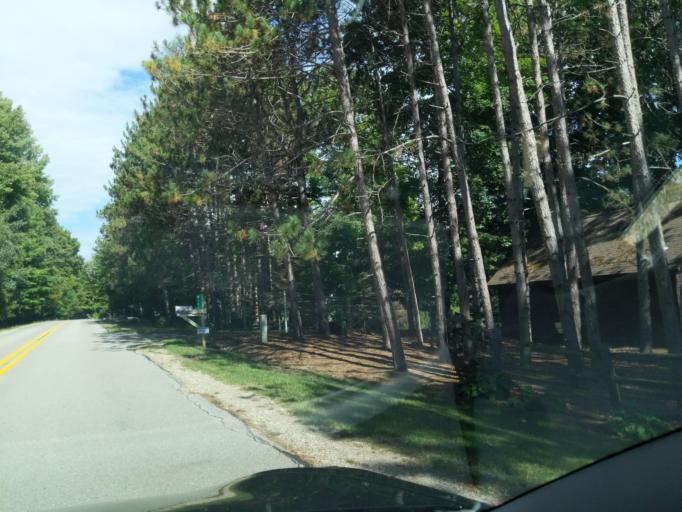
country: US
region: Michigan
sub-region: Antrim County
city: Bellaire
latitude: 44.9701
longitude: -85.3237
